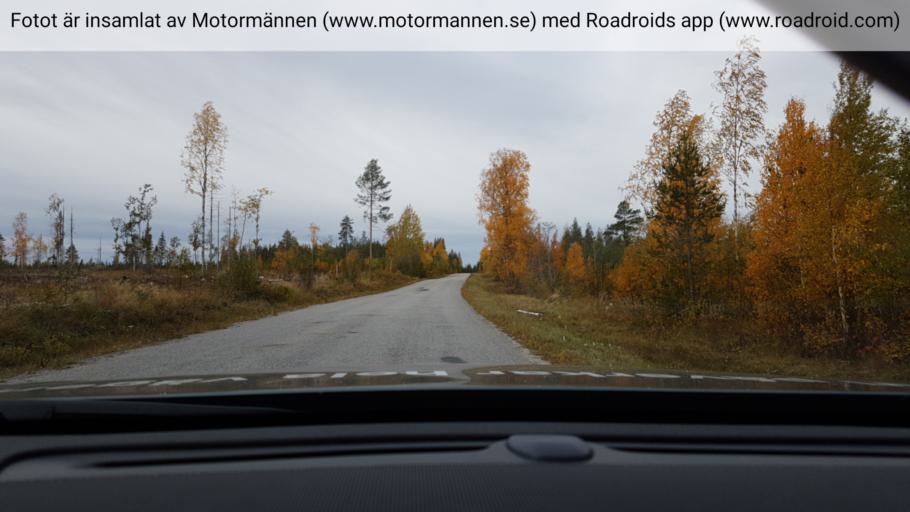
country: SE
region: Norrbotten
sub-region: Overkalix Kommun
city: OEverkalix
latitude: 66.2578
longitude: 23.0665
